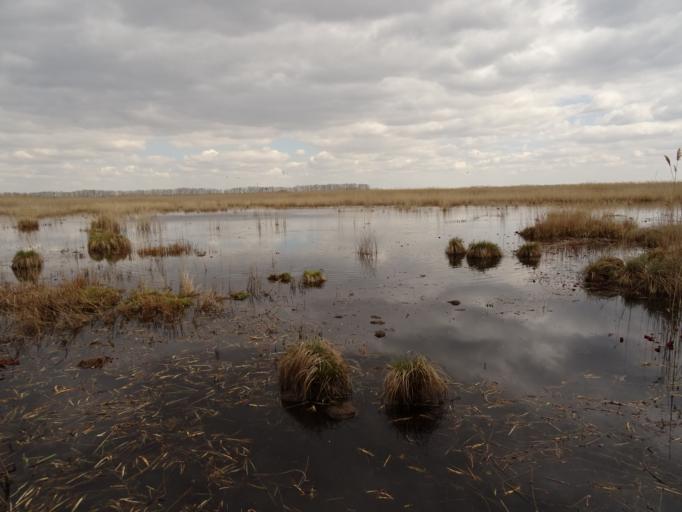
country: HU
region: Bacs-Kiskun
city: Izsak
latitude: 46.7892
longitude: 19.3295
